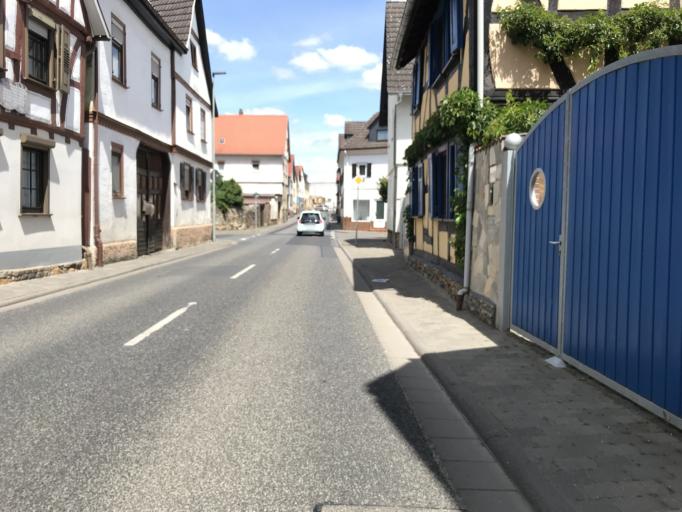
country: DE
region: Hesse
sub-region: Regierungsbezirk Darmstadt
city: Butzbach
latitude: 50.4156
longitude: 8.6824
